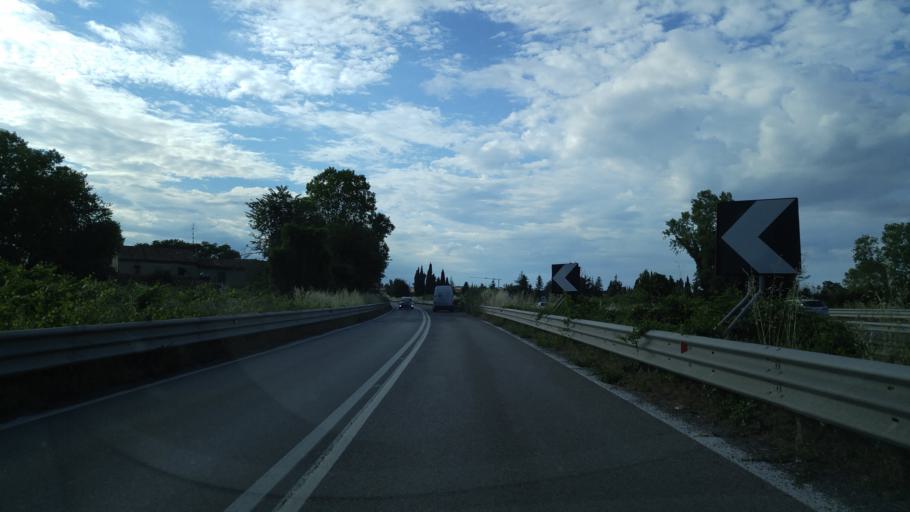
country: IT
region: The Marches
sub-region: Provincia di Pesaro e Urbino
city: Rosciano
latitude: 43.8191
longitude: 13.0161
